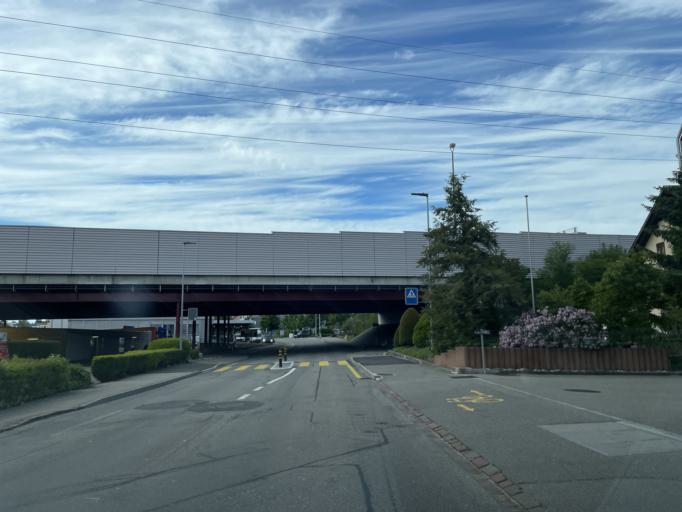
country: CH
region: Zurich
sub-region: Bezirk Uster
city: Bruttisellen
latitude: 47.4184
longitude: 8.6320
